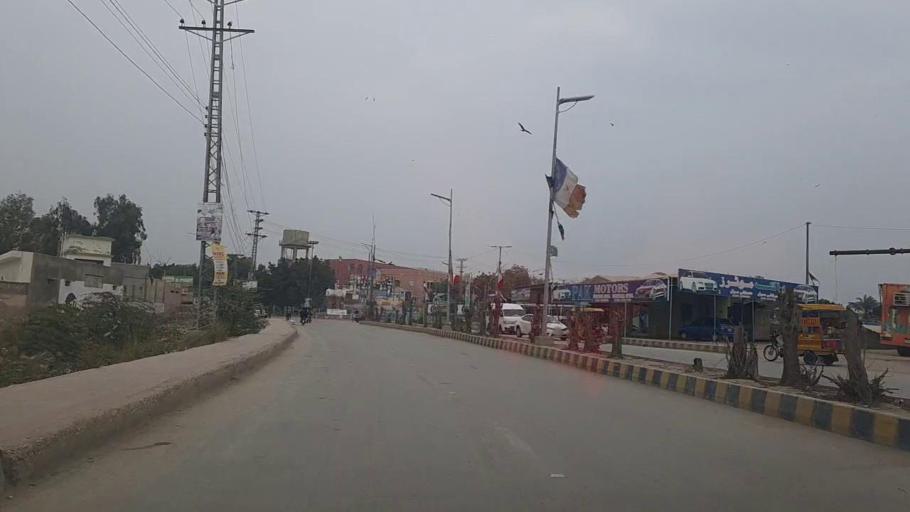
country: PK
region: Sindh
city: Nawabshah
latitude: 26.2411
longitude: 68.4010
